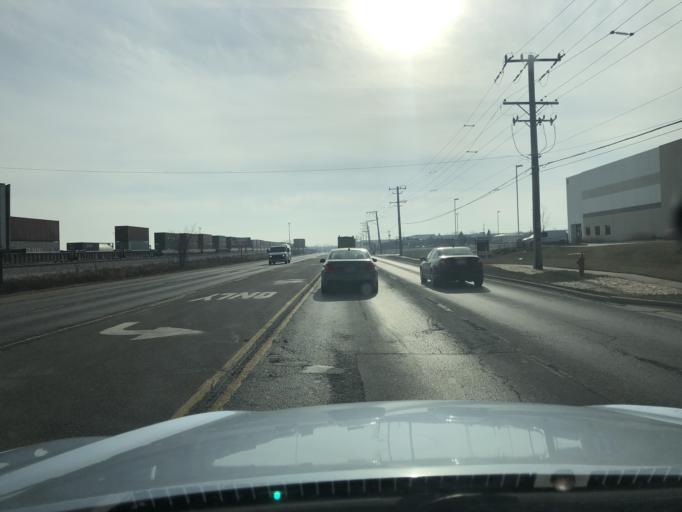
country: US
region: Illinois
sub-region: DuPage County
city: Bensenville
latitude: 41.9678
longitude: -87.9398
